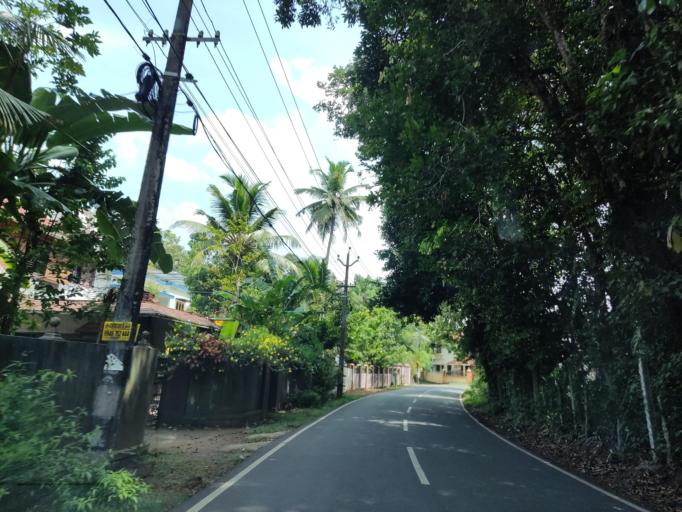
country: IN
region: Kerala
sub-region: Alappuzha
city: Mavelikara
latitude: 9.2828
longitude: 76.5694
